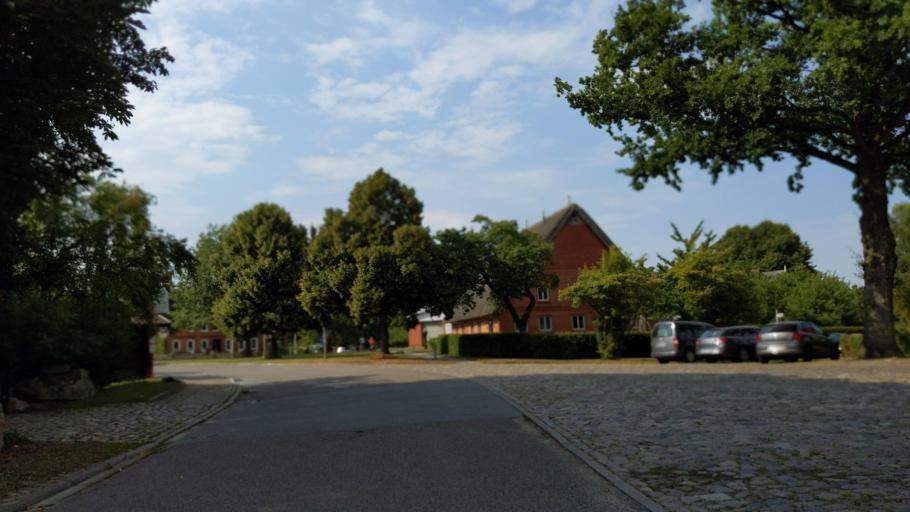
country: DE
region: Schleswig-Holstein
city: Behlendorf
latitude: 53.6988
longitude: 10.6699
